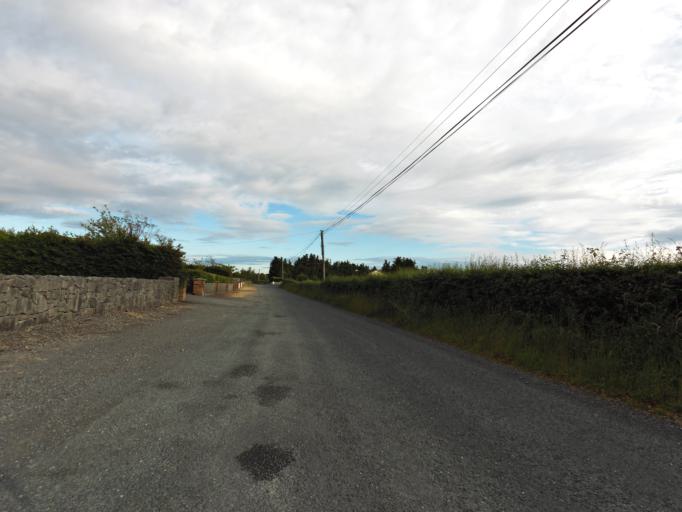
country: IE
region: Connaught
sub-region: County Galway
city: Athenry
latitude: 53.2970
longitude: -8.7345
